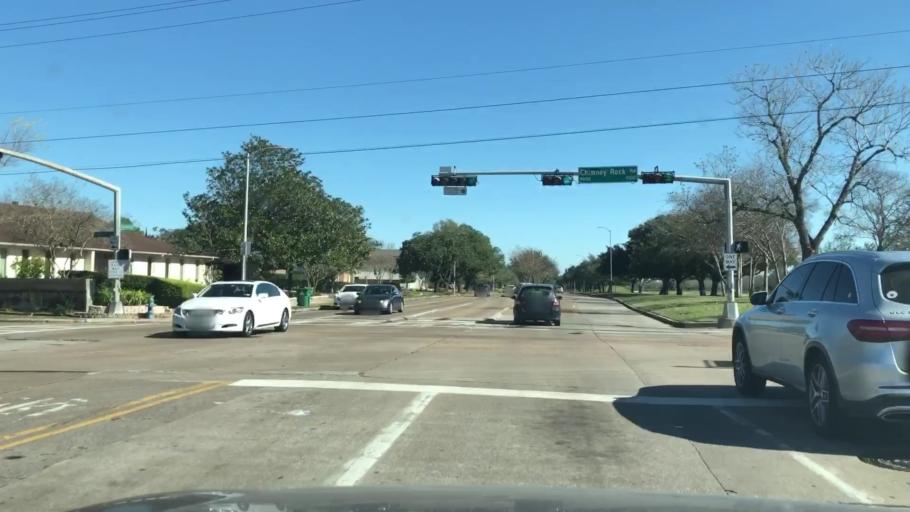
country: US
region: Texas
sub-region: Harris County
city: Bellaire
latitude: 29.6780
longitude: -95.4767
